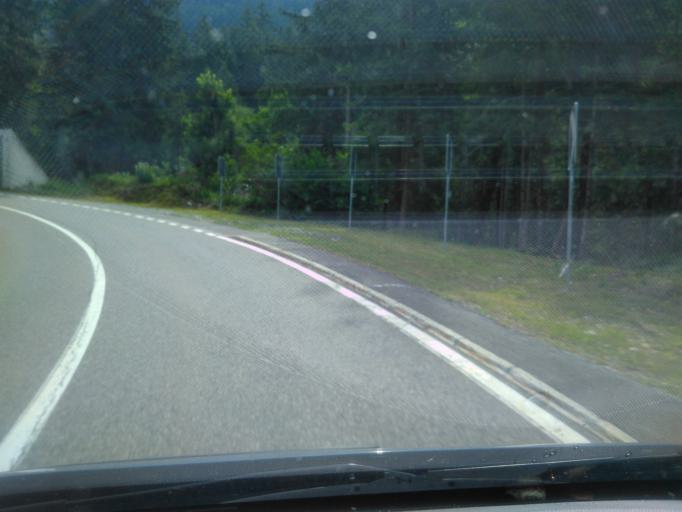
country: CH
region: Obwalden
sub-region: Obwalden
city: Engelberg
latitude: 46.7233
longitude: 8.3241
